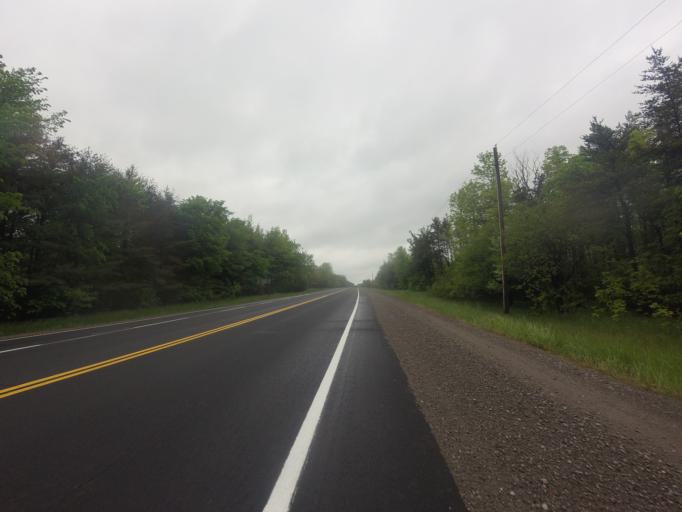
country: CA
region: Ontario
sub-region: Lanark County
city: Smiths Falls
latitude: 44.7895
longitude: -76.1009
